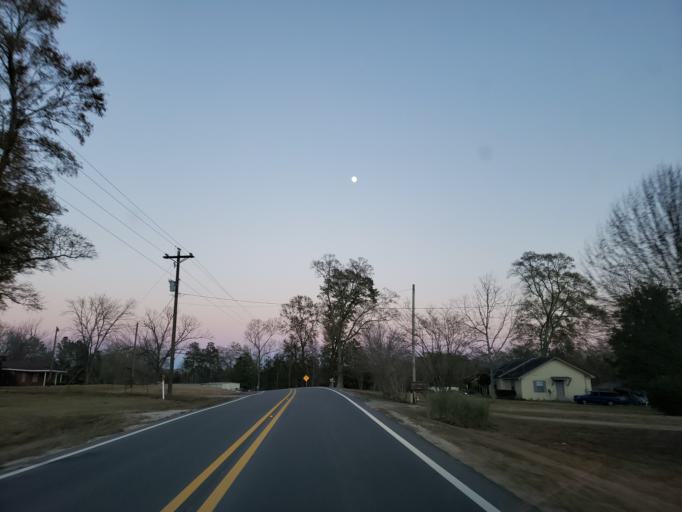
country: US
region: Mississippi
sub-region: Jones County
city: Ellisville
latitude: 31.5825
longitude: -89.2440
